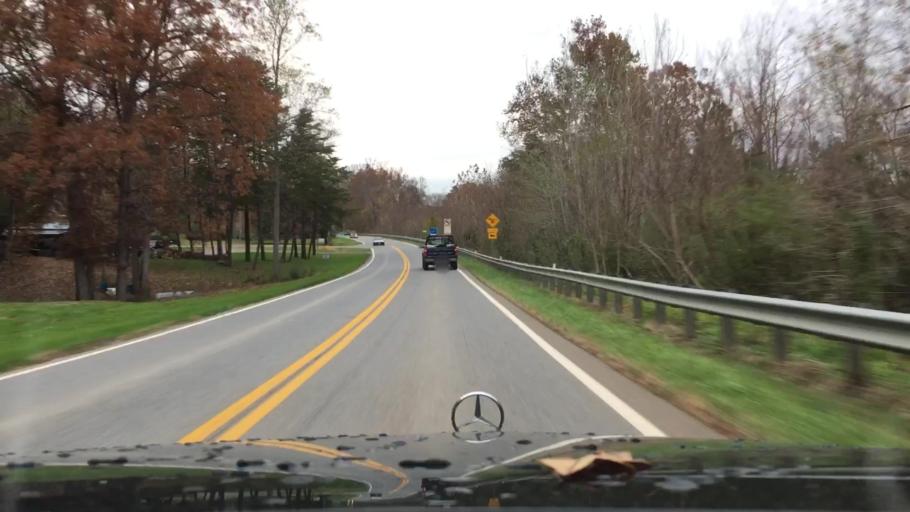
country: US
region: Virginia
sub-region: Campbell County
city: Altavista
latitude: 37.1560
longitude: -79.2975
